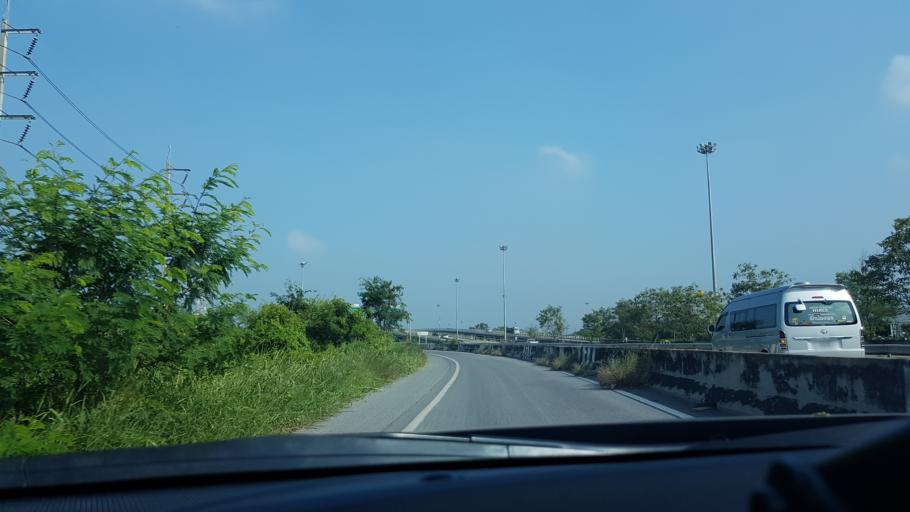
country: TH
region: Phra Nakhon Si Ayutthaya
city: Bang Pa-in
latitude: 14.1525
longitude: 100.5686
